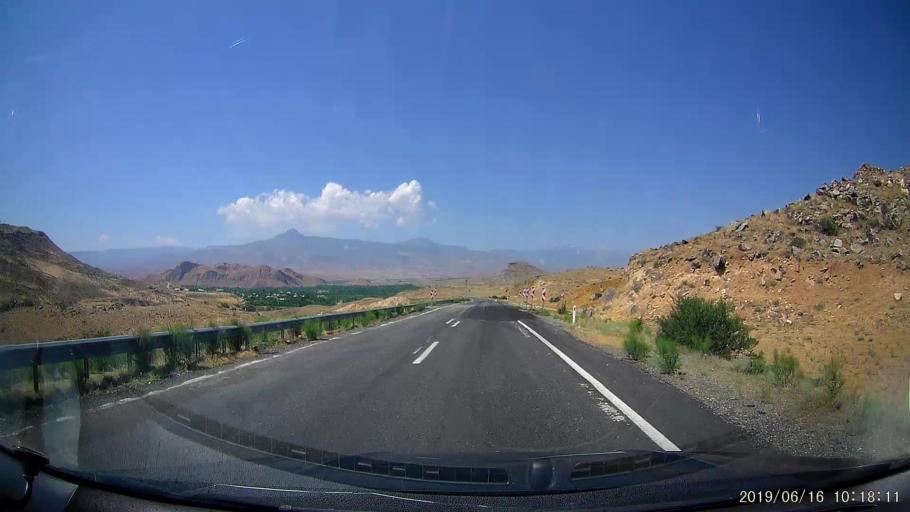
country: TR
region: Igdir
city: Tuzluca
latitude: 40.1627
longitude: 43.6713
